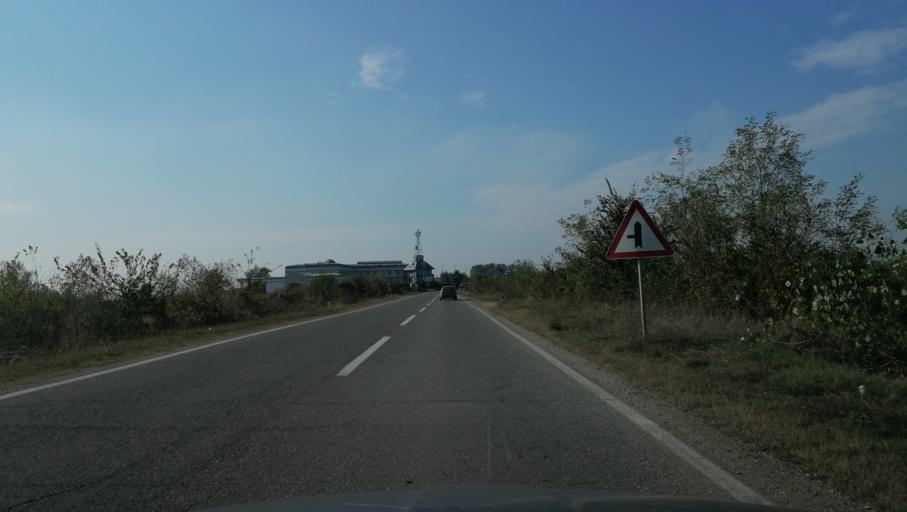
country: BA
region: Republika Srpska
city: Popovi
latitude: 44.7780
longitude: 19.3226
